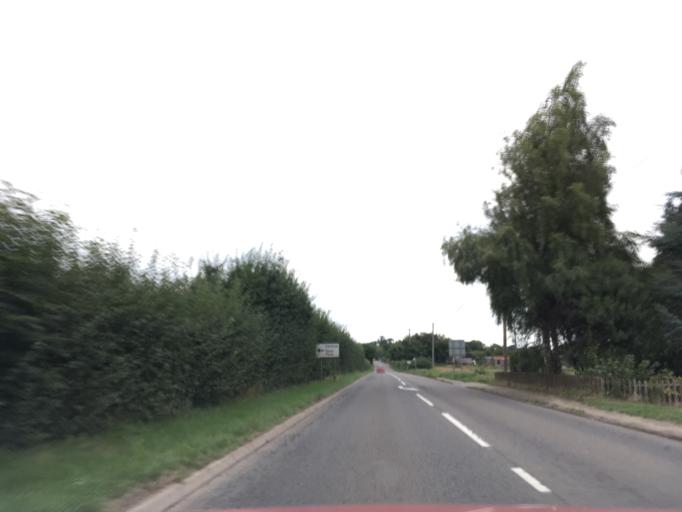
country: GB
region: England
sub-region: Wiltshire
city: Calne
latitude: 51.3973
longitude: -2.0454
